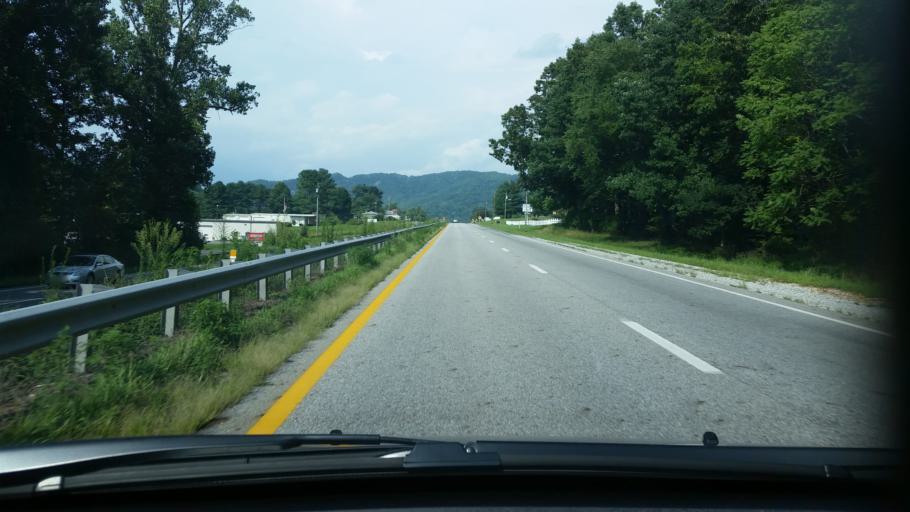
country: US
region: Virginia
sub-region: Nelson County
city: Lovingston
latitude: 37.7443
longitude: -78.8860
